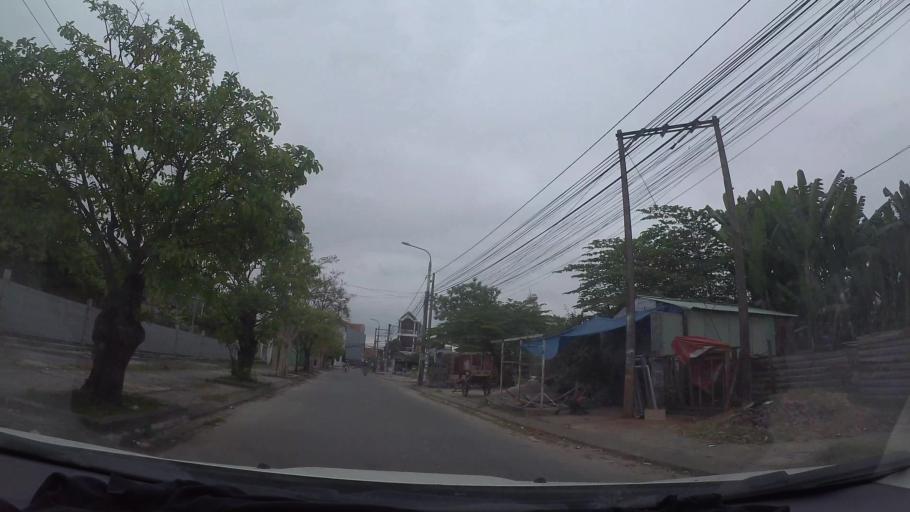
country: VN
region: Da Nang
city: Lien Chieu
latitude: 16.0697
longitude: 108.1438
